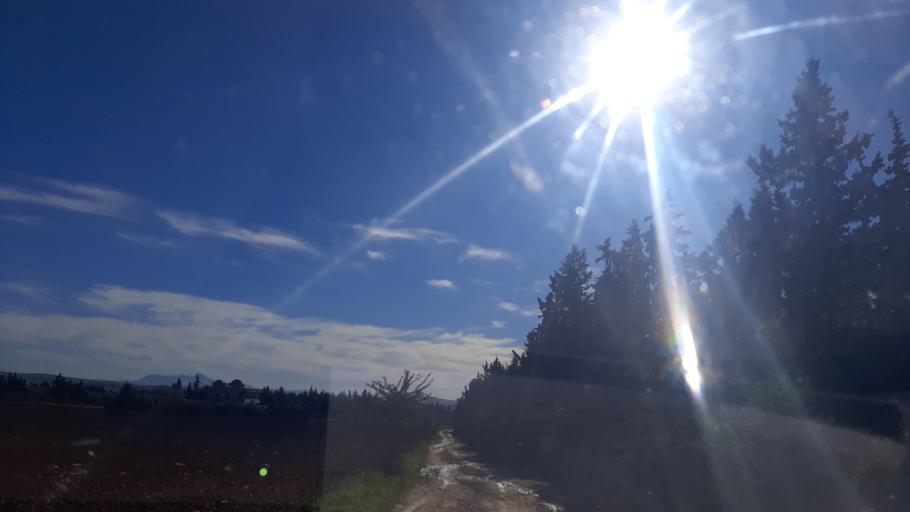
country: TN
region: Tunis
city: Oued Lill
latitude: 36.7604
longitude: 9.9820
